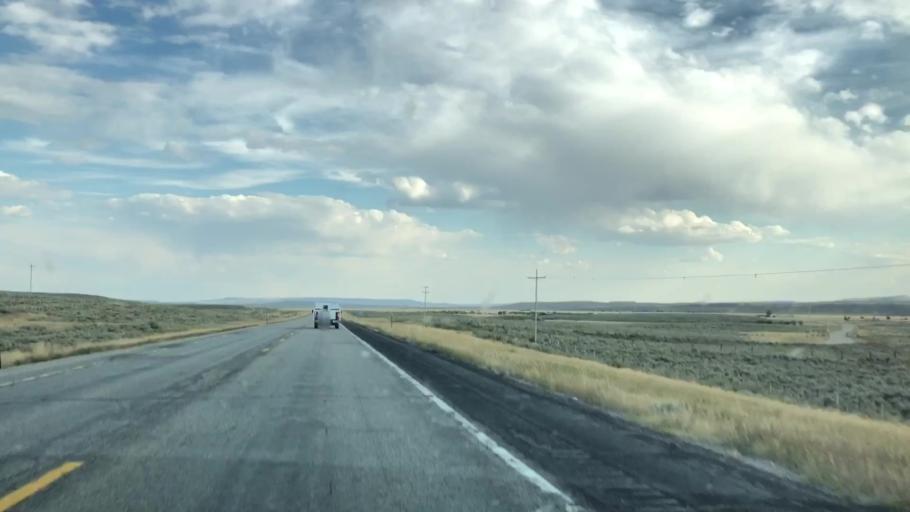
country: US
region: Wyoming
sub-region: Sublette County
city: Pinedale
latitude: 43.0533
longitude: -110.1534
